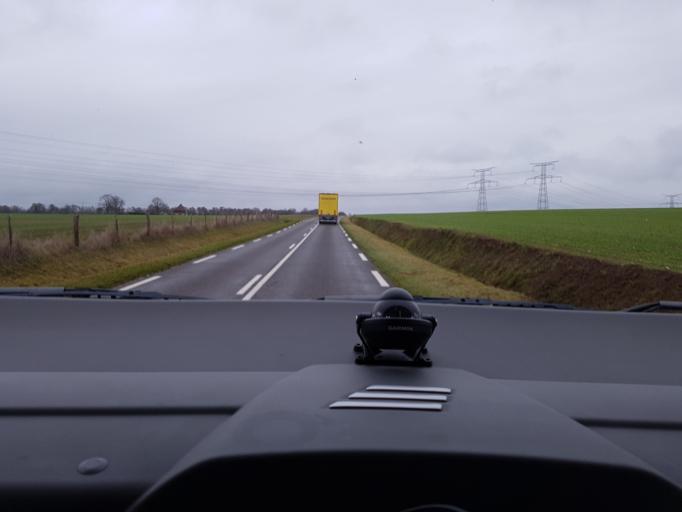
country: FR
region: Haute-Normandie
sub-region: Departement de la Seine-Maritime
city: Gournay-en-Bray
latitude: 49.4505
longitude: 1.6719
